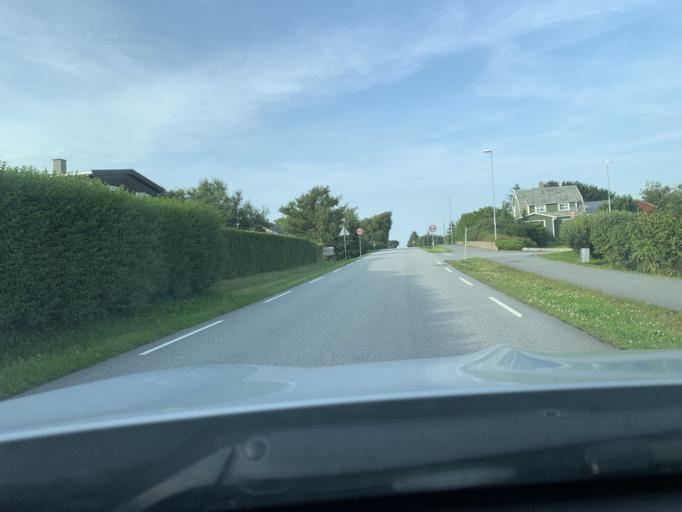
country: NO
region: Rogaland
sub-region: Time
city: Bryne
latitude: 58.7201
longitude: 5.5721
